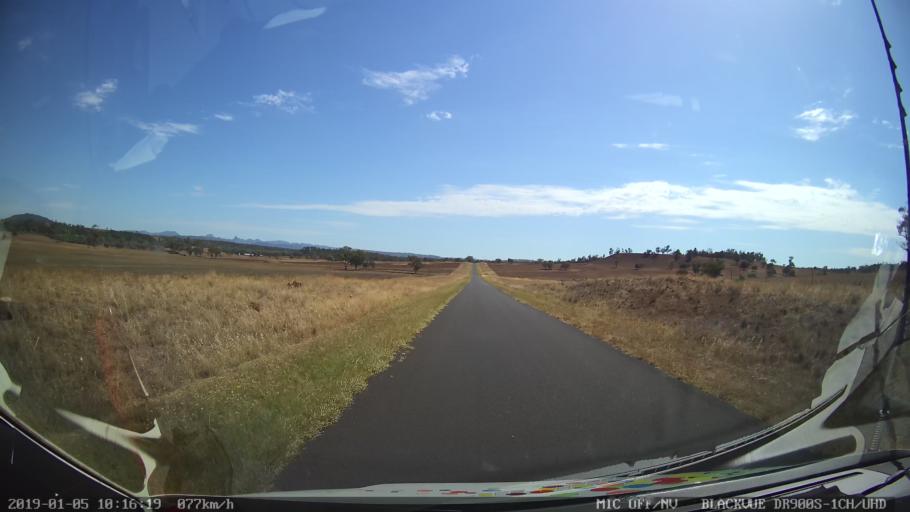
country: AU
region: New South Wales
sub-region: Gilgandra
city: Gilgandra
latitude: -31.5764
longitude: 148.9512
